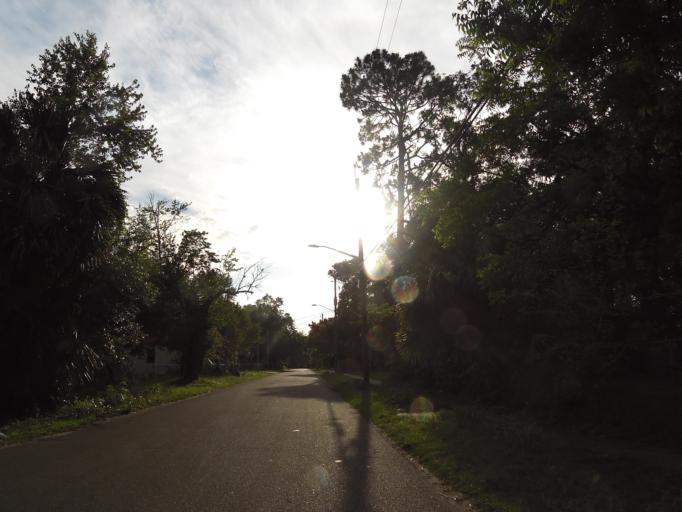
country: US
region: Florida
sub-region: Duval County
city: Jacksonville
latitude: 30.3548
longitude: -81.6649
